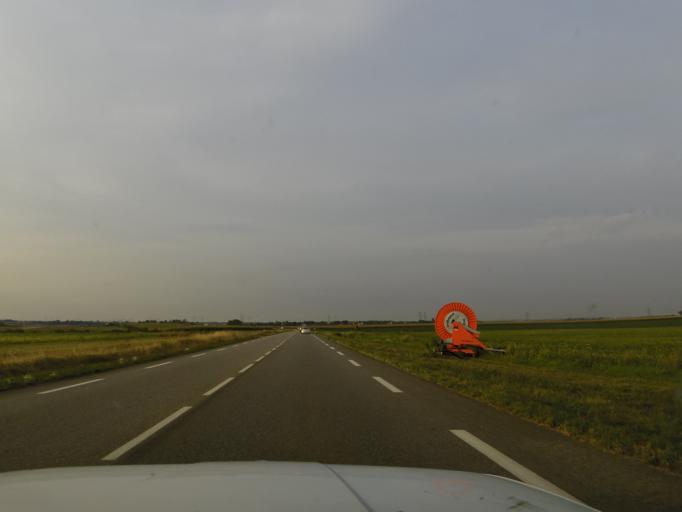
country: FR
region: Rhone-Alpes
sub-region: Departement de l'Ain
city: Perouges
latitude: 45.8766
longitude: 5.1830
